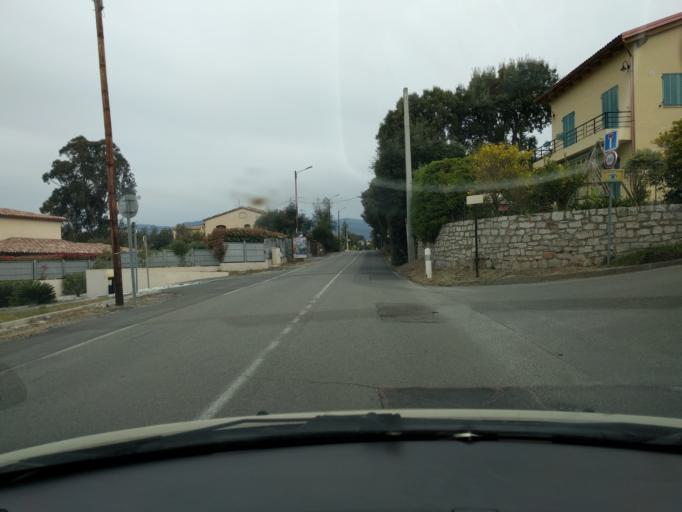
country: FR
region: Provence-Alpes-Cote d'Azur
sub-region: Departement des Alpes-Maritimes
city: La Roquette-sur-Siagne
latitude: 43.5908
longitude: 6.9572
